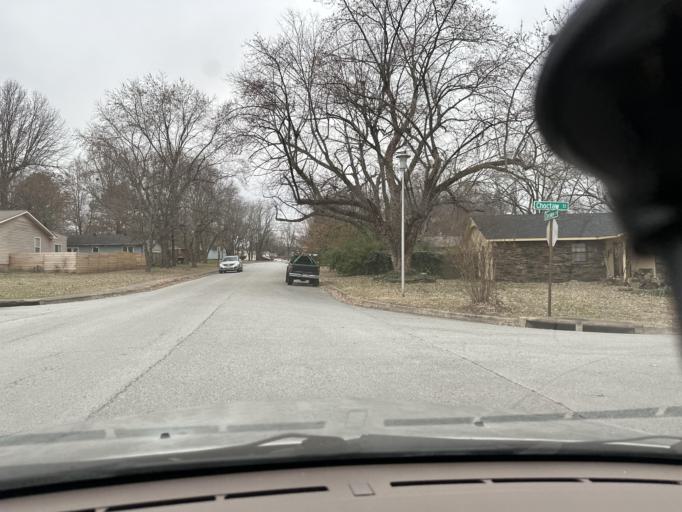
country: US
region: Arkansas
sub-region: Washington County
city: Fayetteville
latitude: 36.0858
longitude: -94.1142
